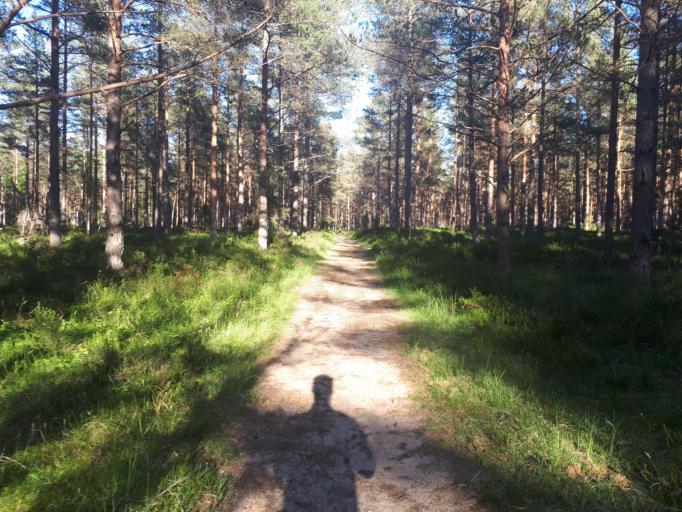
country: SE
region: Gotland
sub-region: Gotland
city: Visby
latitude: 57.6080
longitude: 18.2925
